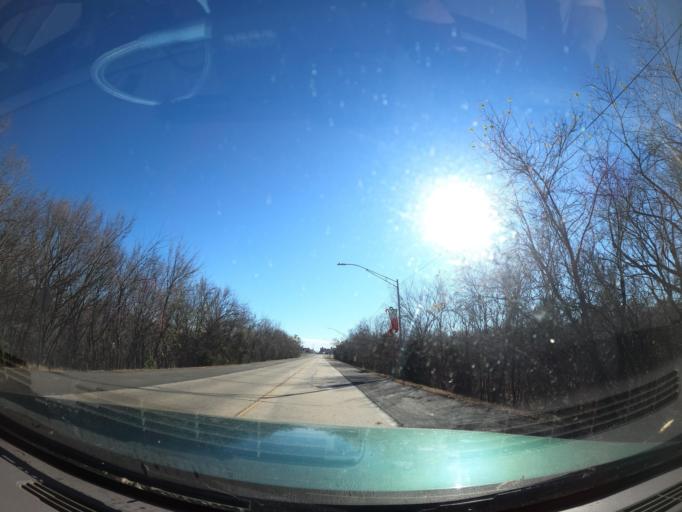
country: US
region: Oklahoma
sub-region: McIntosh County
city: Eufaula
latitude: 35.2929
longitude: -95.5823
